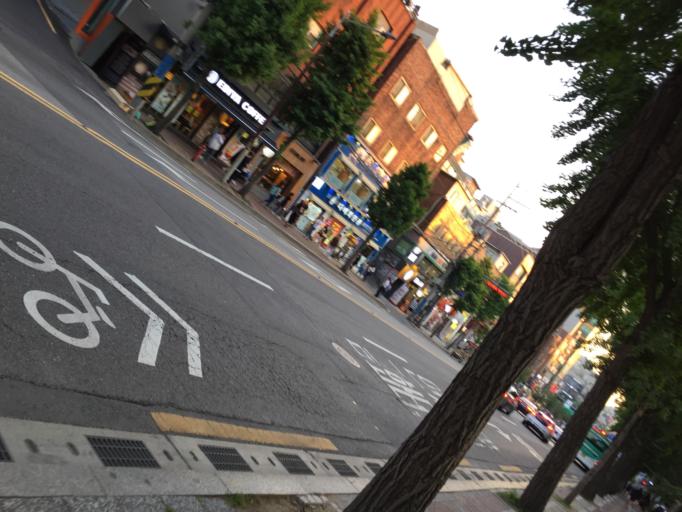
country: KR
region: Seoul
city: Seoul
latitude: 37.5593
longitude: 126.9416
